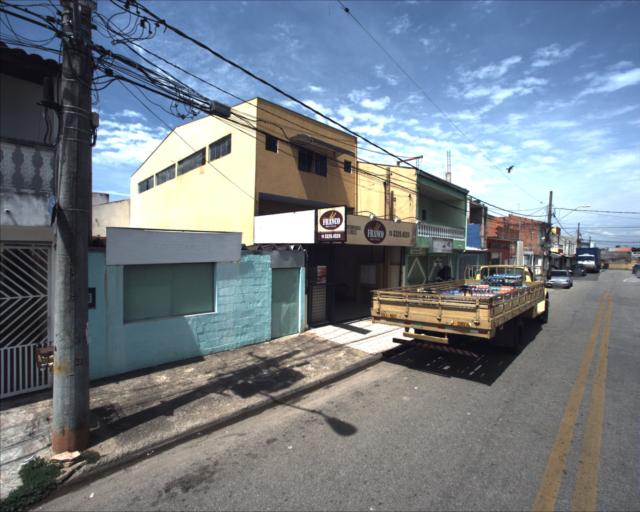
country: BR
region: Sao Paulo
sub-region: Sorocaba
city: Sorocaba
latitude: -23.4136
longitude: -47.4107
